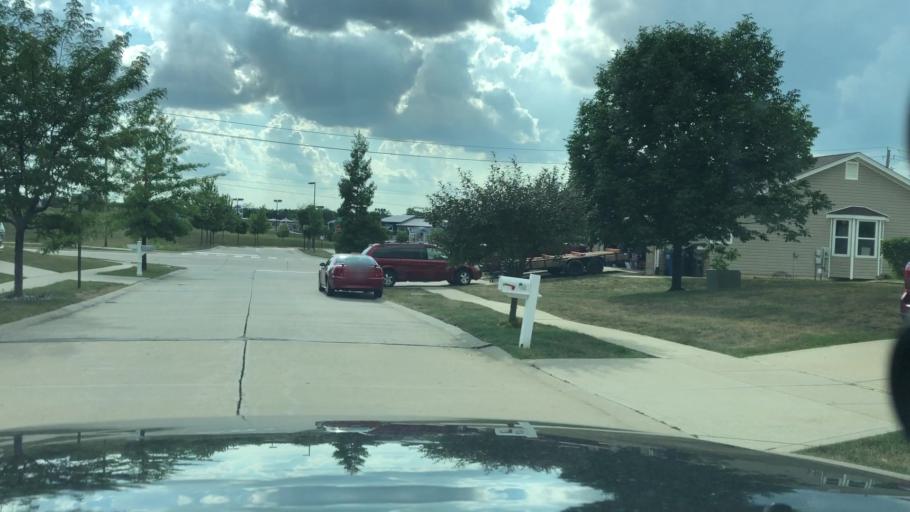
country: US
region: Missouri
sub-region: Saint Charles County
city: Wentzville
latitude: 38.8378
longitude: -90.8914
